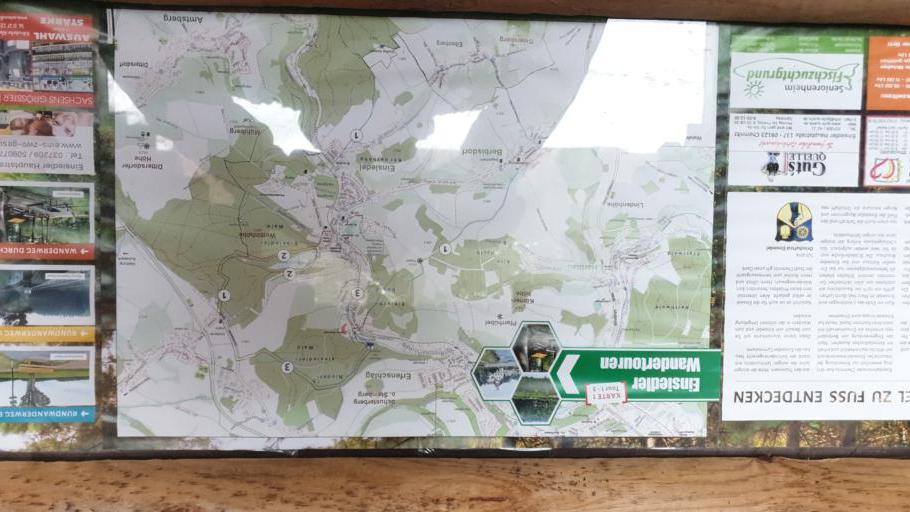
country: DE
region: Saxony
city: Gornau
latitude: 50.7706
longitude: 12.9915
